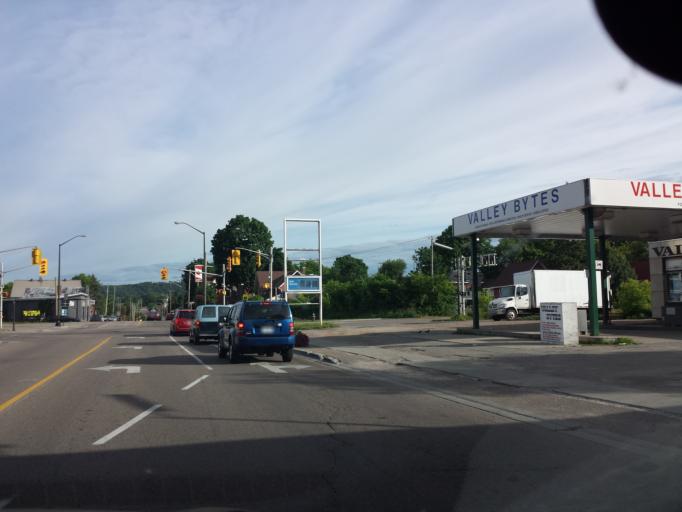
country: CA
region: Ontario
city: Renfrew
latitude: 45.4744
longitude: -76.6872
